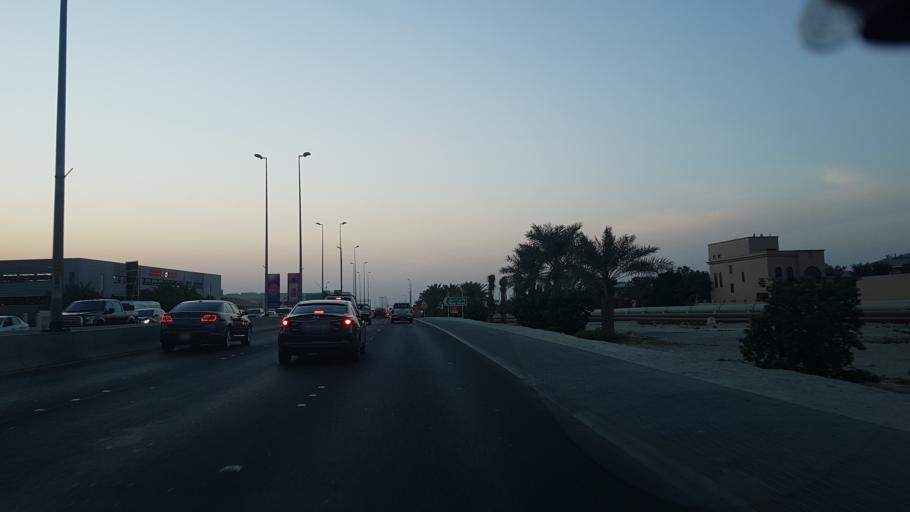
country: BH
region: Central Governorate
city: Madinat Hamad
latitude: 26.1369
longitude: 50.5255
